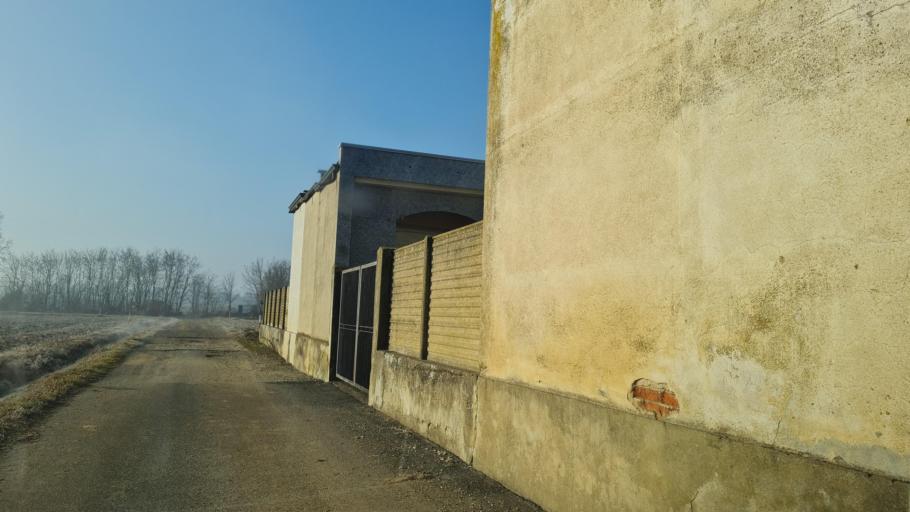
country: IT
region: Piedmont
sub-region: Provincia di Biella
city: Salussola
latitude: 45.4443
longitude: 8.1488
